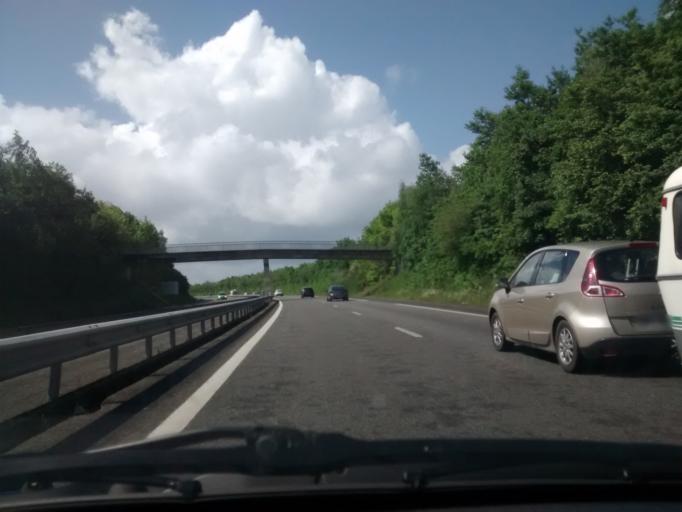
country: FR
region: Brittany
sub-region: Departement d'Ille-et-Vilaine
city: Plelan-le-Grand
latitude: 47.9985
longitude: -2.0944
